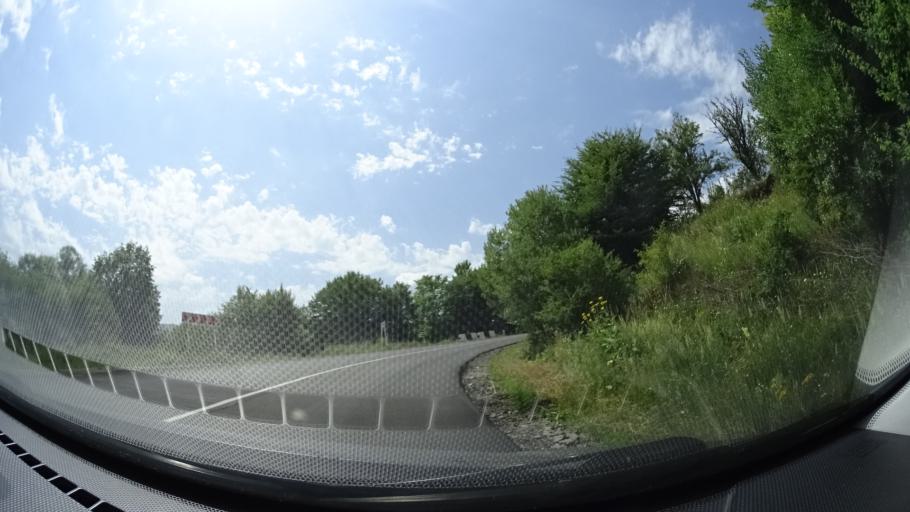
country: GE
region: Kakheti
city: Sagarejo
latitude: 41.8611
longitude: 45.3186
